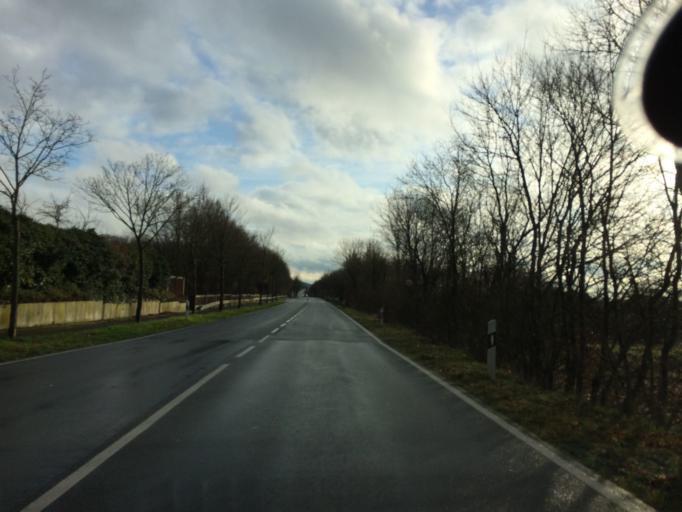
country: DE
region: North Rhine-Westphalia
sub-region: Regierungsbezirk Munster
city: Haltern
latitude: 51.7178
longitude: 7.1228
